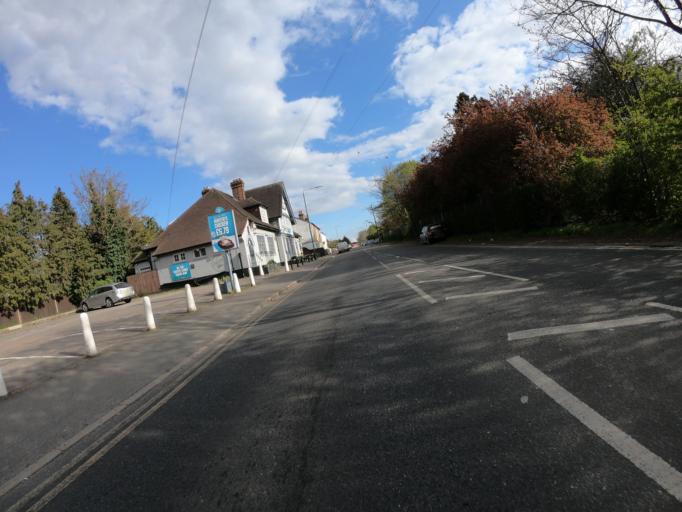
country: GB
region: England
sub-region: Greater London
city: Bexleyheath
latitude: 51.4637
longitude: 0.1507
